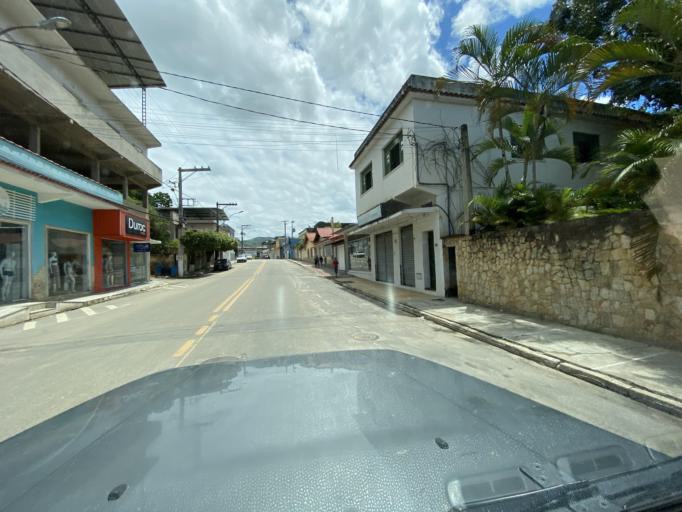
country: BR
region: Espirito Santo
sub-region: Jeronimo Monteiro
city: Jeronimo Monteiro
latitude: -20.7901
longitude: -41.3970
